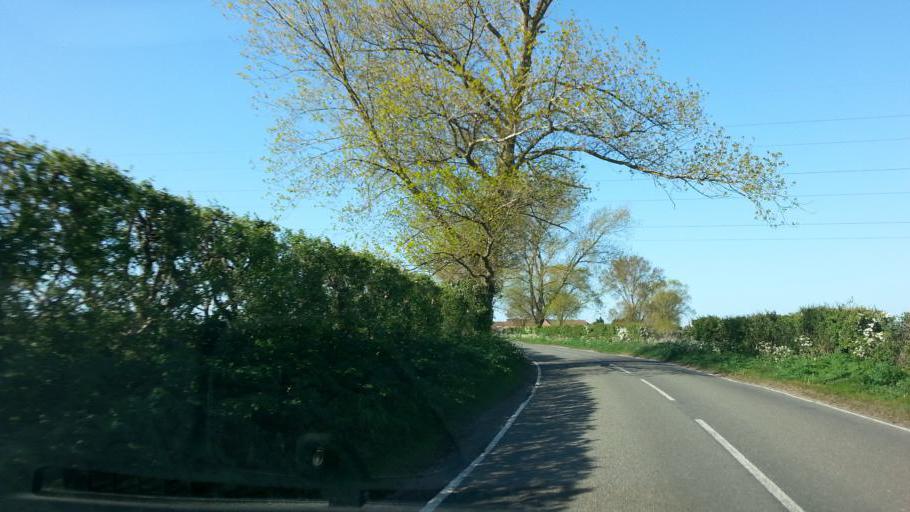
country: GB
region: England
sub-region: Lincolnshire
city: Great Gonerby
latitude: 52.9730
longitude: -0.6837
